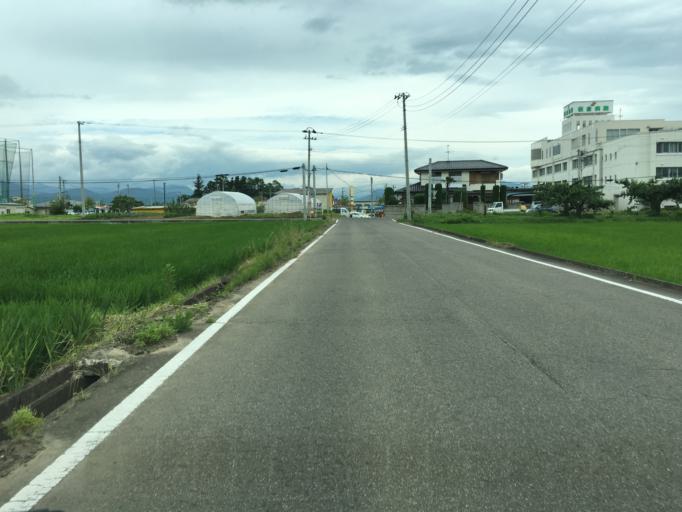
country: JP
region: Fukushima
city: Fukushima-shi
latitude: 37.7387
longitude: 140.4369
